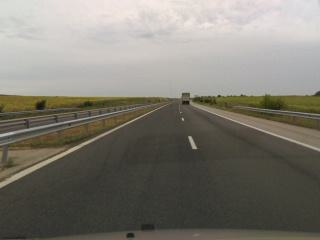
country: BG
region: Stara Zagora
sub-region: Obshtina Chirpan
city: Chirpan
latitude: 42.2410
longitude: 25.3777
